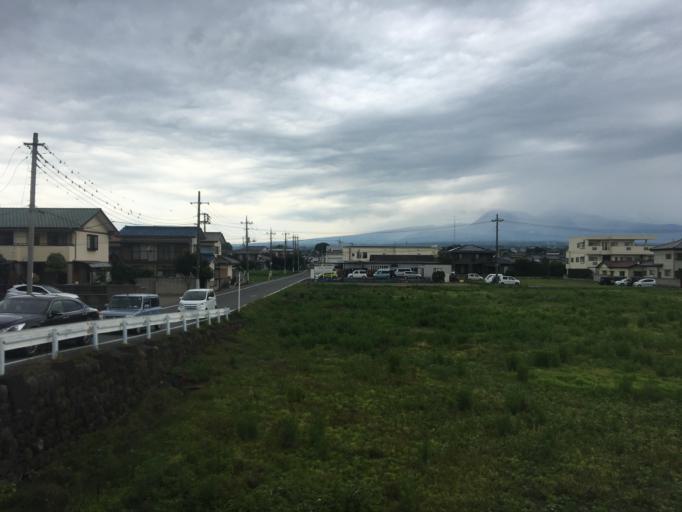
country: JP
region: Gunma
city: Maebashi-shi
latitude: 36.3943
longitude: 139.1091
